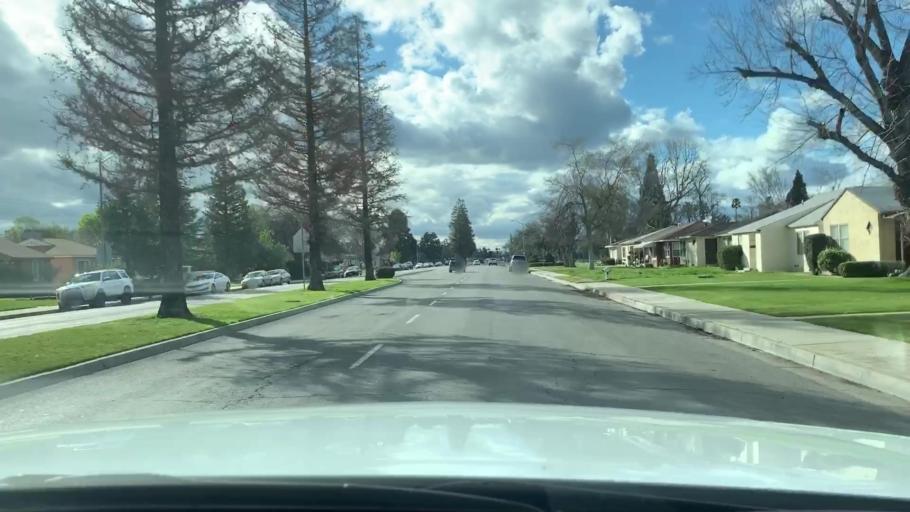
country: US
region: California
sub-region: Kern County
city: Bakersfield
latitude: 35.3735
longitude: -119.0327
